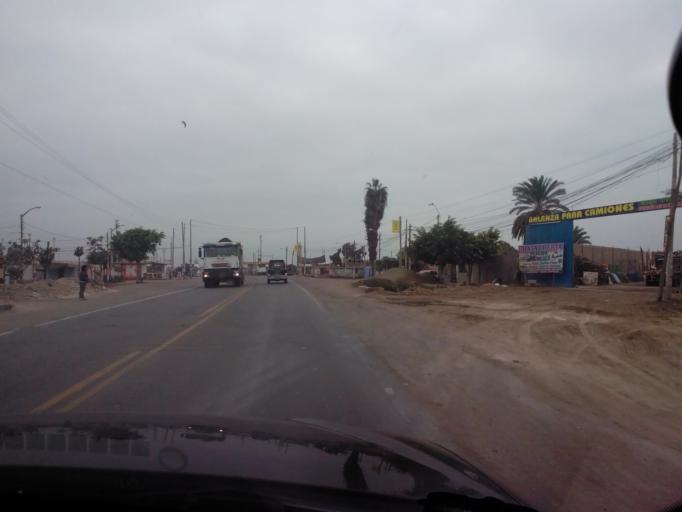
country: PE
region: Ica
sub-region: Provincia de Pisco
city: Villa Tupac Amaru
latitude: -13.7046
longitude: -76.1510
